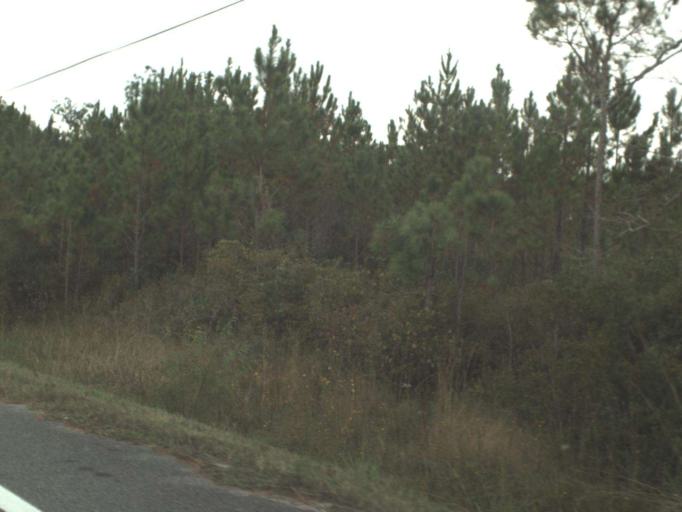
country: US
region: Florida
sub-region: Wakulla County
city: Crawfordville
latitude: 30.0663
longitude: -84.4642
